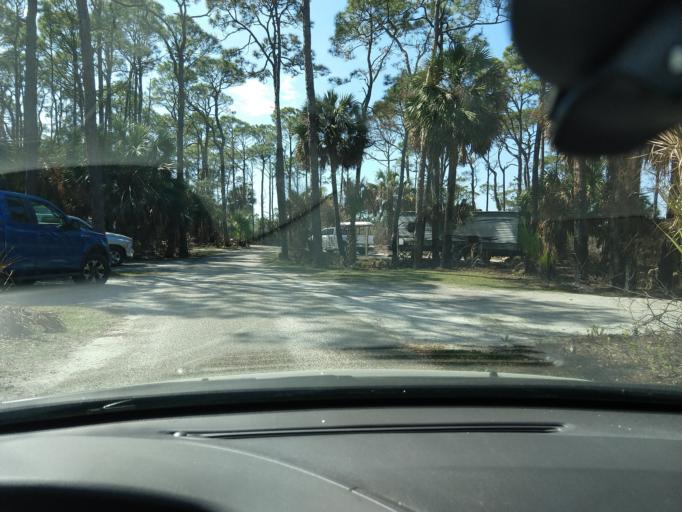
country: US
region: Florida
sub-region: Gulf County
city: Port Saint Joe
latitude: 29.7813
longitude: -85.4066
